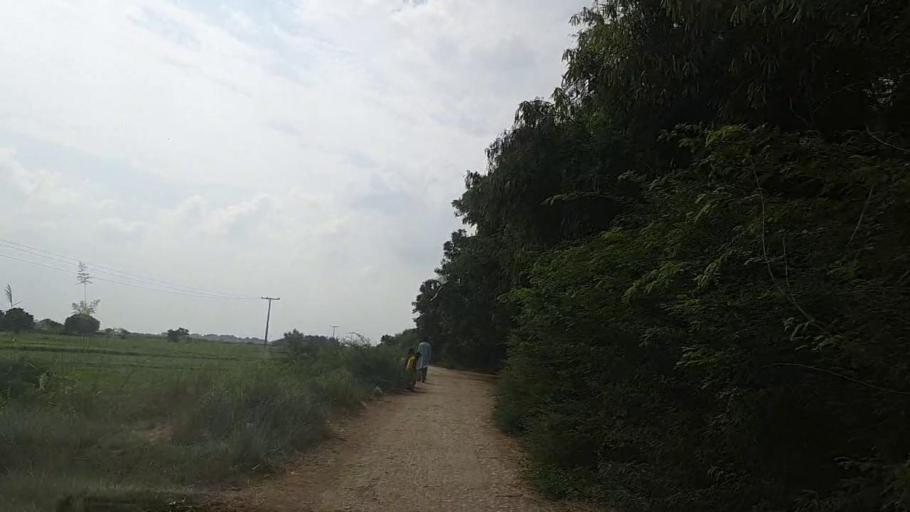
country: PK
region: Sindh
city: Mirpur Batoro
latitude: 24.5934
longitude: 68.1287
